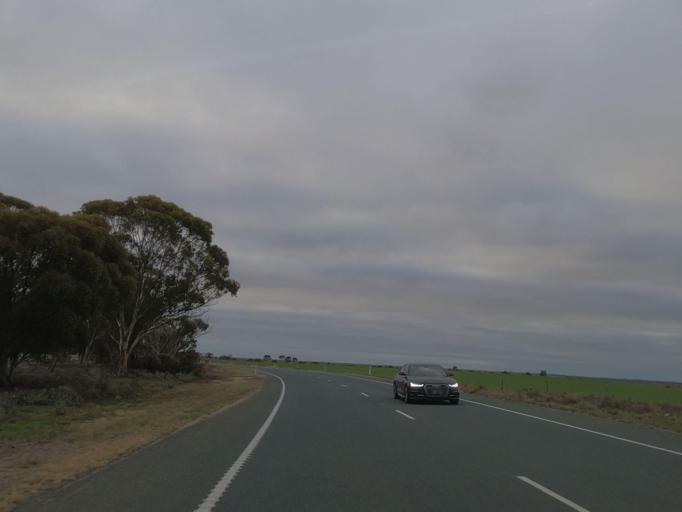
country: AU
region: Victoria
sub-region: Swan Hill
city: Swan Hill
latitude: -35.5630
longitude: 143.7827
